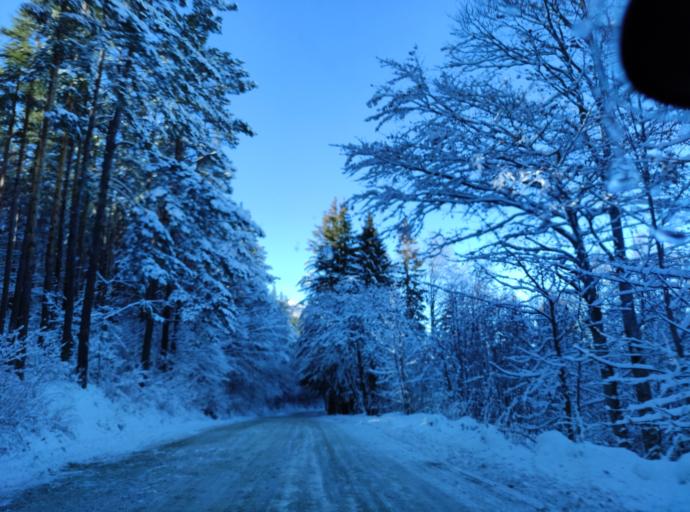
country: BG
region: Sofia-Capital
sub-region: Stolichna Obshtina
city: Sofia
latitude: 42.5951
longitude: 23.3101
